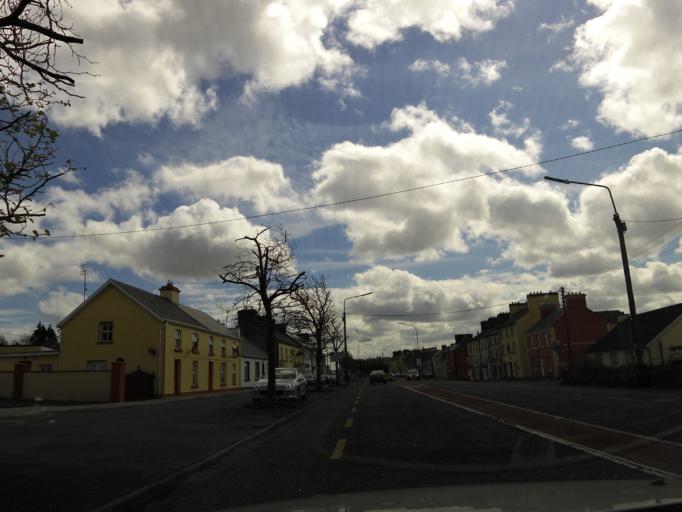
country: IE
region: Connaught
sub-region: Maigh Eo
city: Claremorris
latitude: 53.6703
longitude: -8.9579
